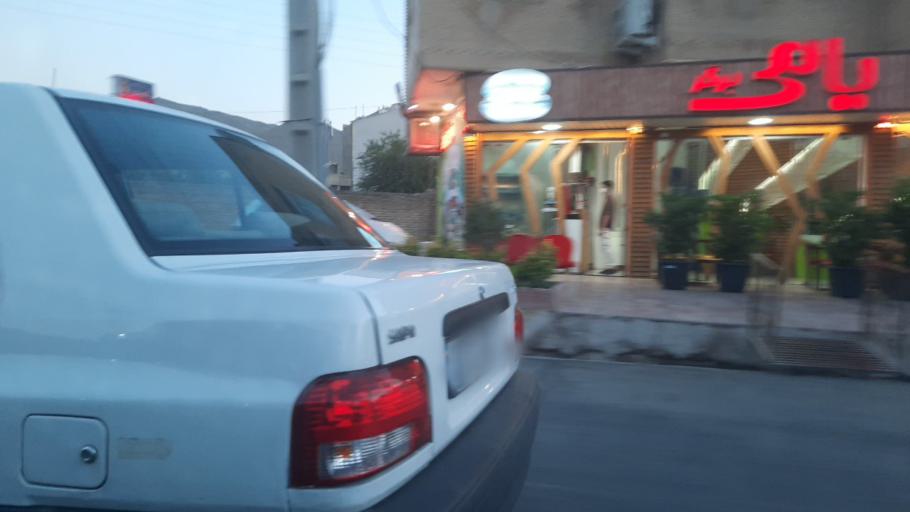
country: IR
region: Markazi
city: Arak
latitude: 34.0769
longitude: 49.6974
